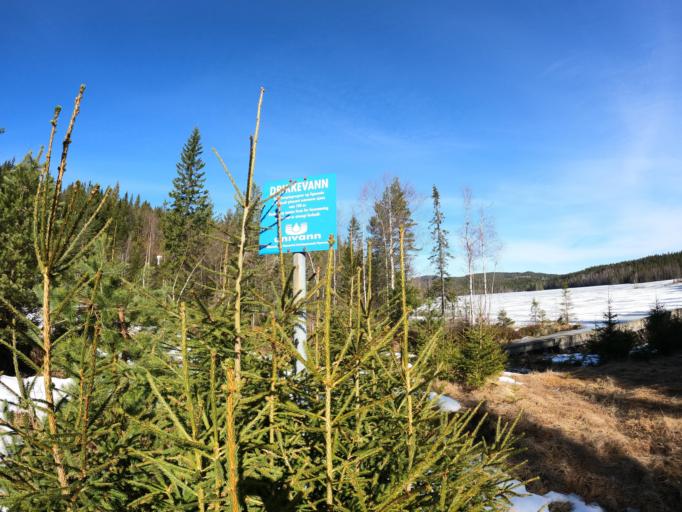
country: NO
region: Akershus
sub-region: Nittedal
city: Aneby
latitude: 60.1894
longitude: 10.8850
